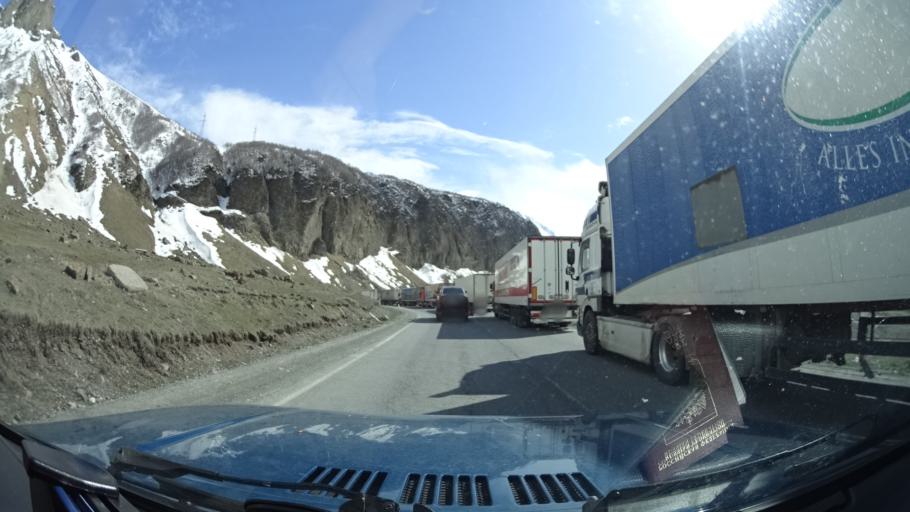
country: GE
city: Gudauri
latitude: 42.5683
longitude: 44.5202
